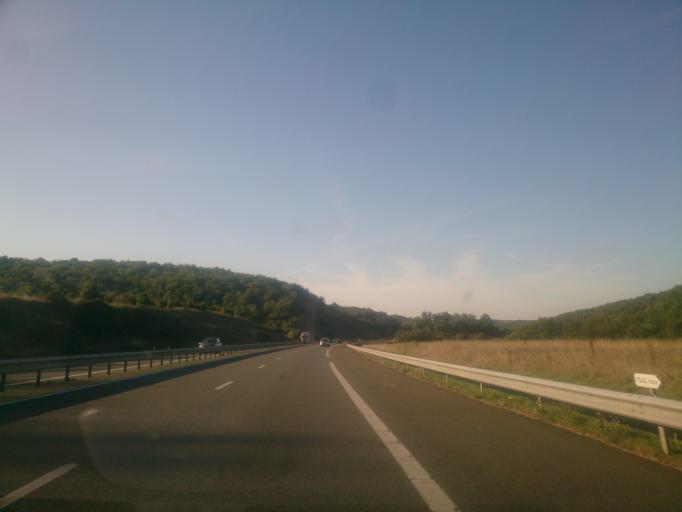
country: FR
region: Midi-Pyrenees
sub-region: Departement du Lot
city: Le Vigan
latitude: 44.7534
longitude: 1.5407
